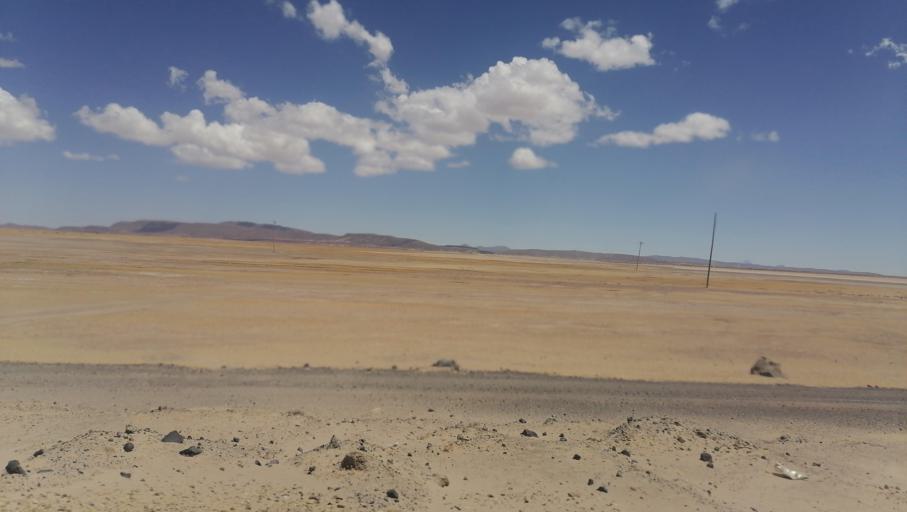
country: BO
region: Oruro
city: Challapata
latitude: -19.2137
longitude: -67.0225
